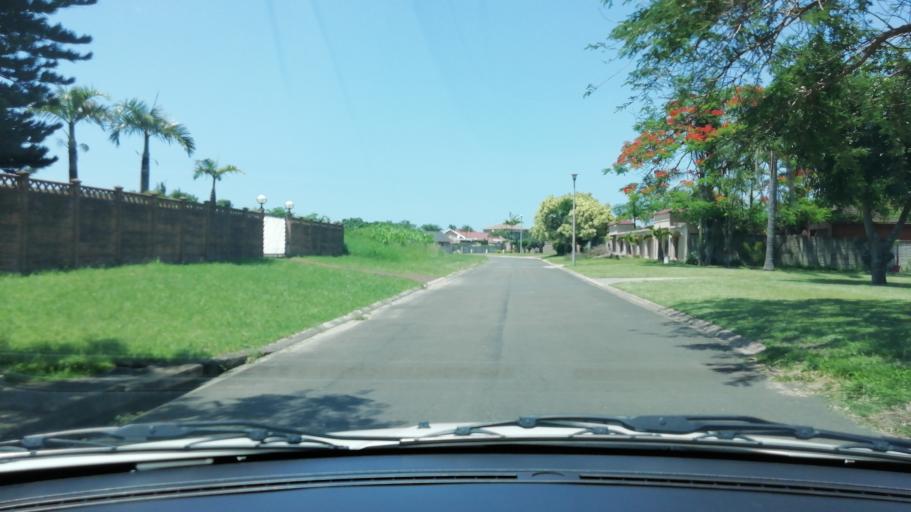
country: ZA
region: KwaZulu-Natal
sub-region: uThungulu District Municipality
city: Richards Bay
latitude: -28.7335
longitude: 32.0525
